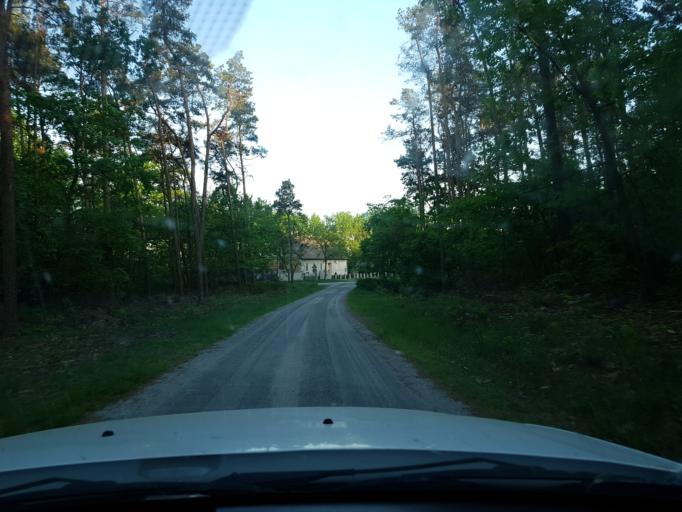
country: PL
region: West Pomeranian Voivodeship
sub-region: Powiat stargardzki
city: Kobylanka
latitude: 53.3911
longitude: 14.8991
